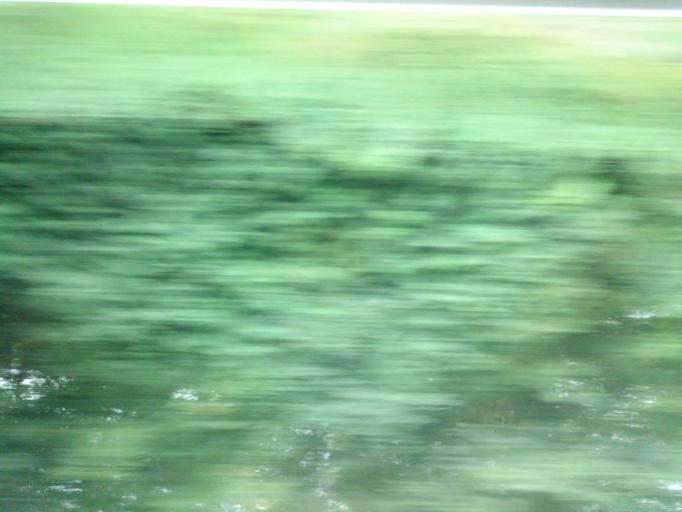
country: DE
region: Mecklenburg-Vorpommern
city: Ferdinandshof
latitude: 53.6756
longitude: 13.8854
